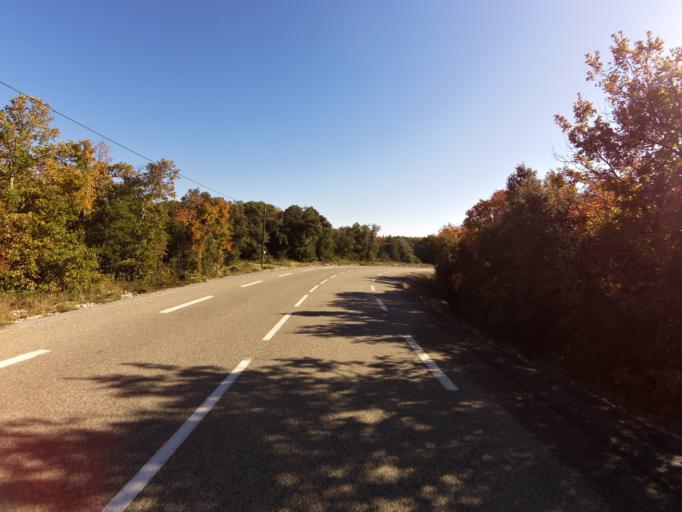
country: FR
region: Rhone-Alpes
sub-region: Departement de l'Ardeche
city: Ruoms
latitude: 44.4007
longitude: 4.4712
